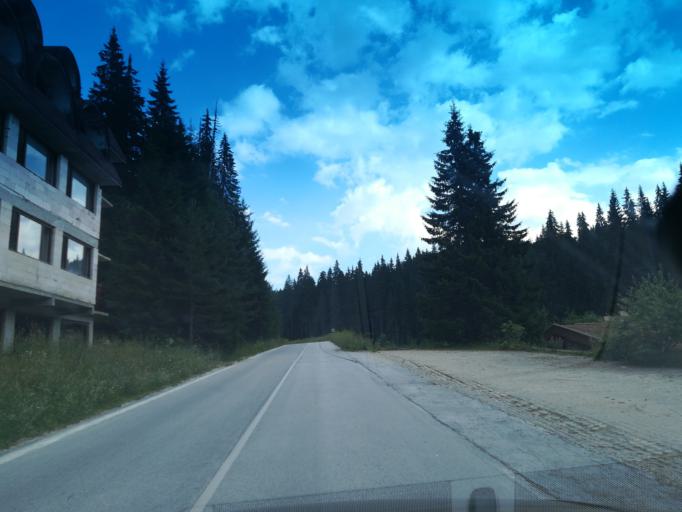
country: BG
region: Smolyan
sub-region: Obshtina Smolyan
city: Smolyan
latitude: 41.6575
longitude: 24.6838
